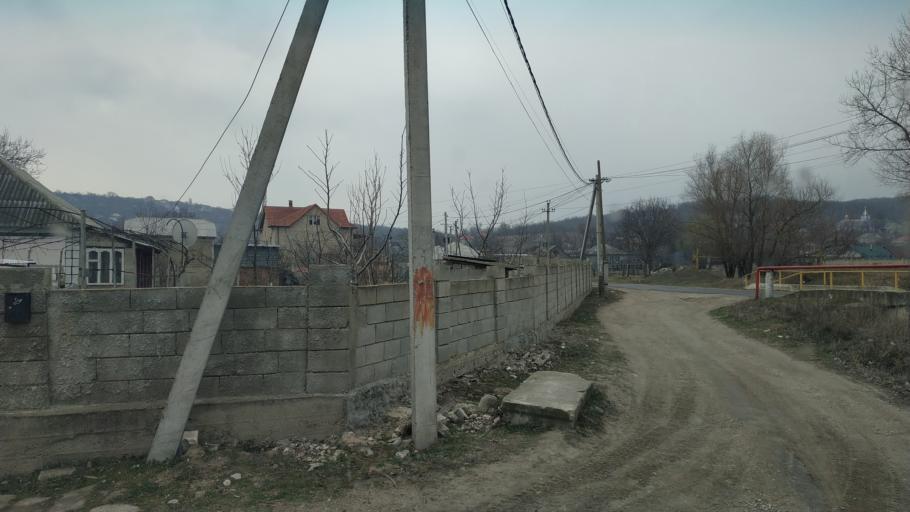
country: MD
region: Chisinau
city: Singera
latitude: 46.9143
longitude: 28.9756
